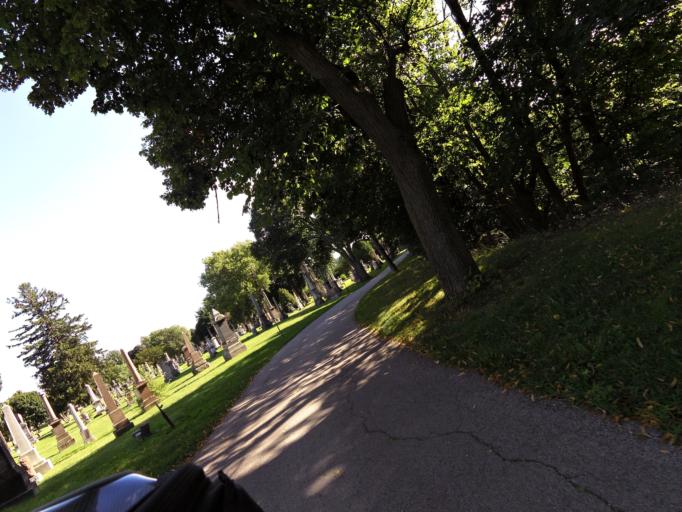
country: CA
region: Ontario
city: Hamilton
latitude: 43.2710
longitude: -79.8883
